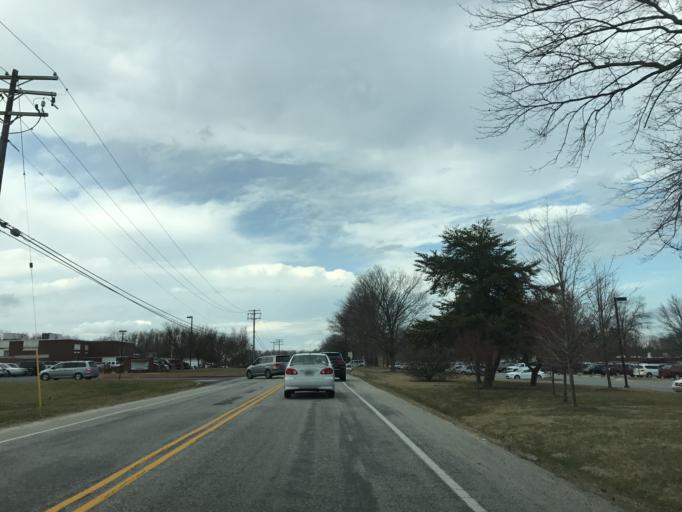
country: US
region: Maryland
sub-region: Harford County
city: South Bel Air
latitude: 39.5578
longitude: -76.2863
